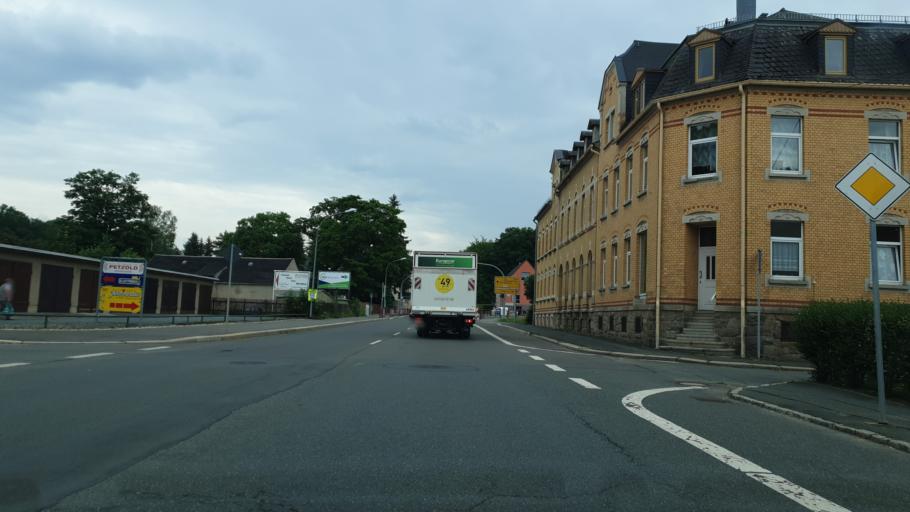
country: DE
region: Saxony
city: Rodewisch
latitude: 50.5365
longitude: 12.4007
